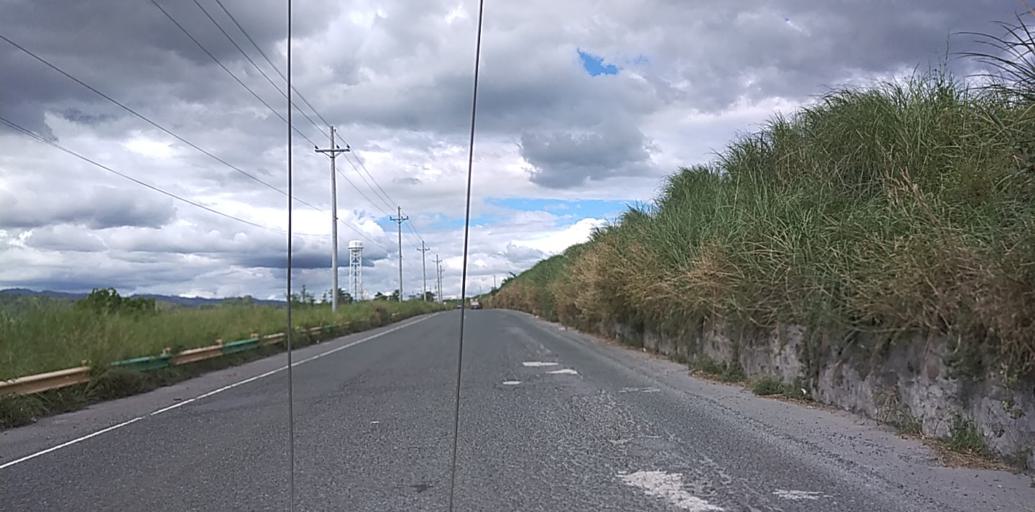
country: PH
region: Central Luzon
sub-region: Province of Pampanga
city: Dolores
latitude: 15.1084
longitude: 120.5195
